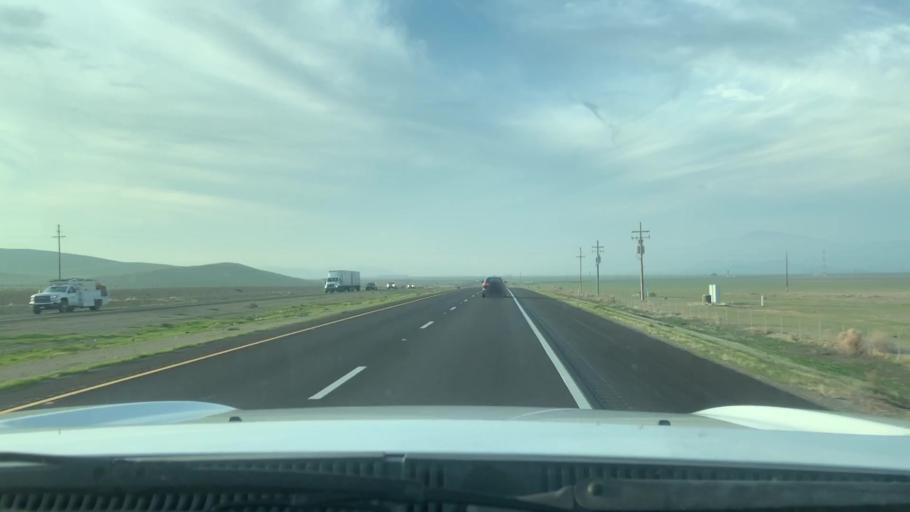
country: US
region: California
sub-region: Kern County
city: Lost Hills
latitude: 35.6467
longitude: -120.0308
